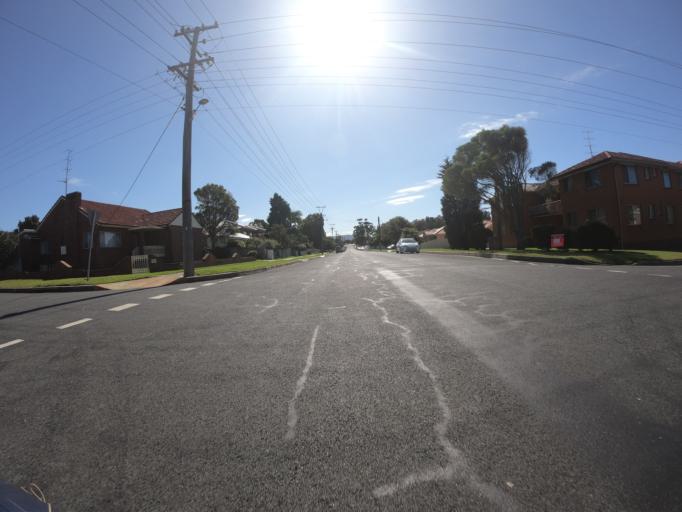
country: AU
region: New South Wales
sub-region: Wollongong
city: East Corrimal
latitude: -34.3724
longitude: 150.9077
